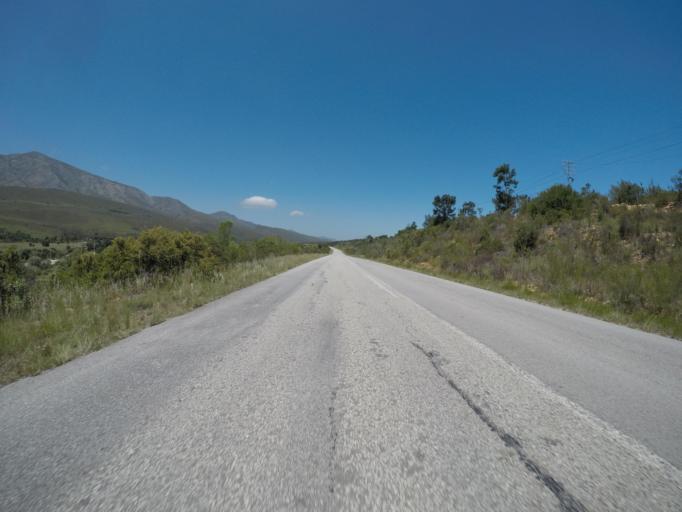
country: ZA
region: Eastern Cape
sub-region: Cacadu District Municipality
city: Kareedouw
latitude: -33.9129
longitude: 24.1726
